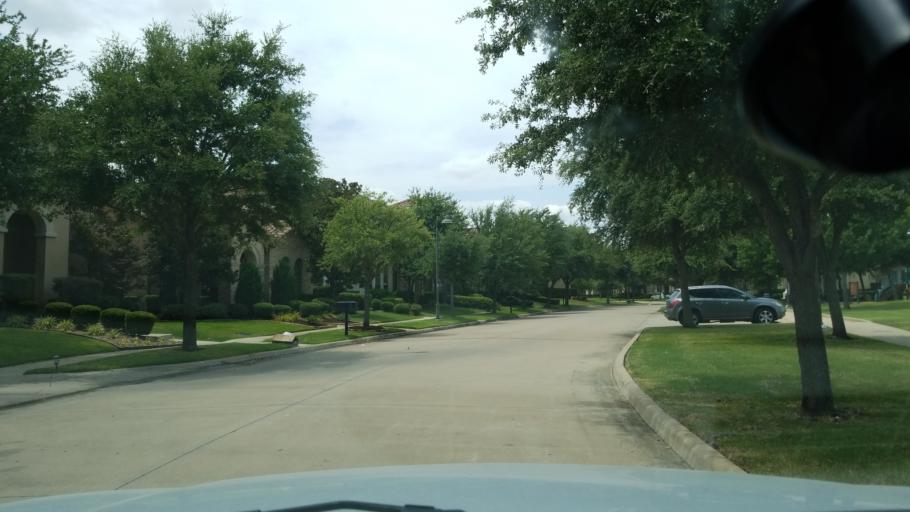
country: US
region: Texas
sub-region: Dallas County
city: Farmers Branch
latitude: 32.9027
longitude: -96.9292
